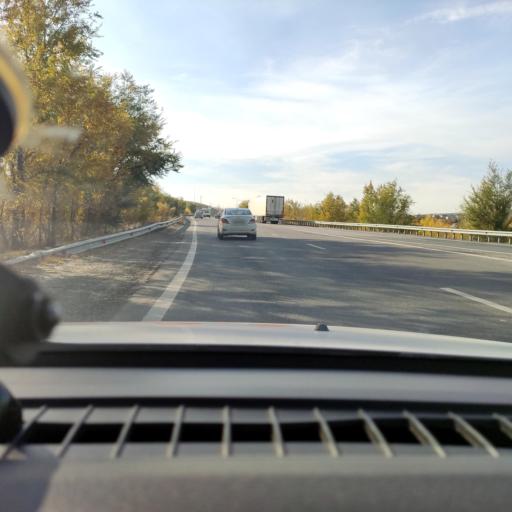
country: RU
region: Samara
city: Novosemeykino
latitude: 53.4104
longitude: 50.3377
